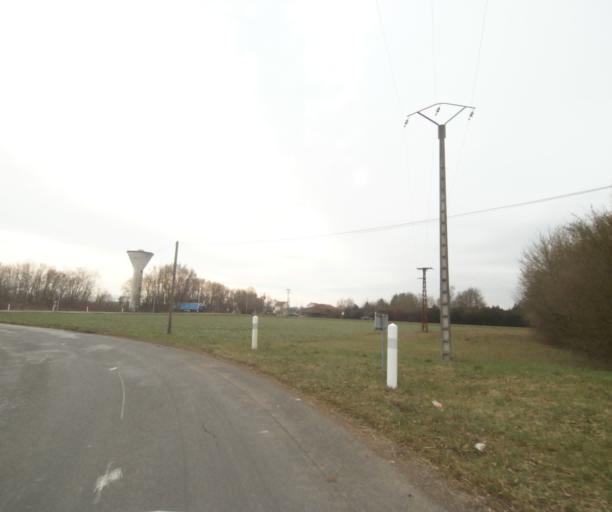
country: FR
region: Champagne-Ardenne
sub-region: Departement de la Haute-Marne
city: Villiers-en-Lieu
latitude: 48.6485
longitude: 4.8736
